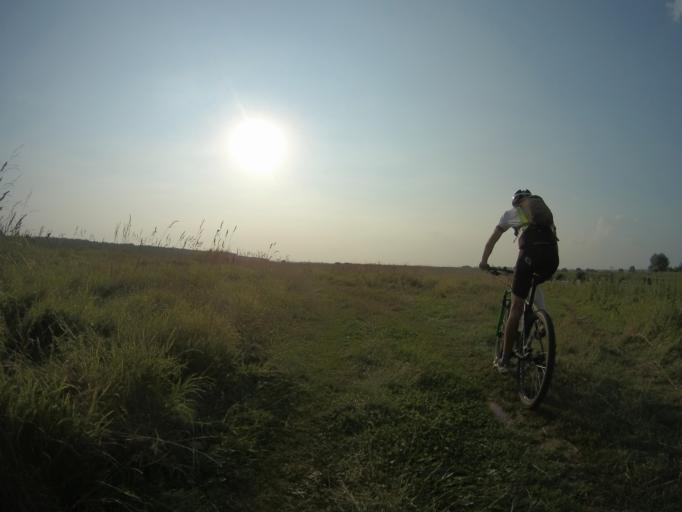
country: RU
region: Vladimir
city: Orgtrud
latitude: 56.2999
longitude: 40.6767
